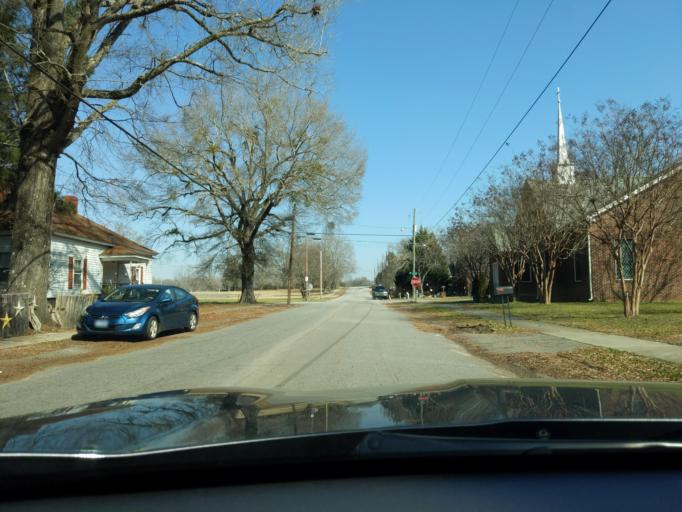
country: US
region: South Carolina
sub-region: Abbeville County
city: Calhoun Falls
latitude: 34.0921
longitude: -82.5912
